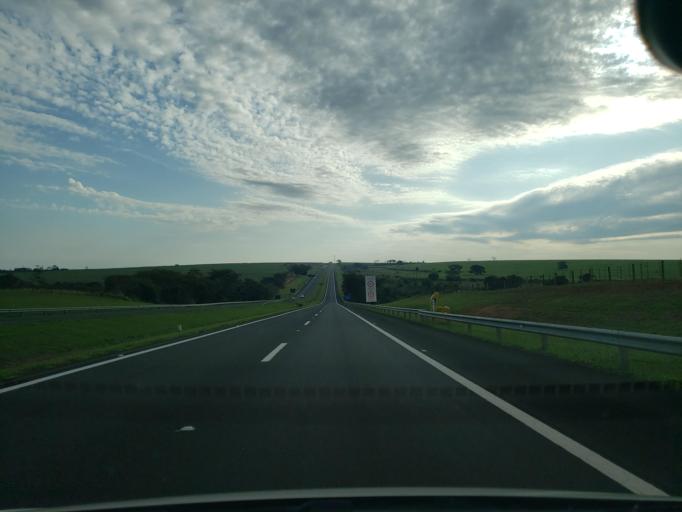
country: BR
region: Sao Paulo
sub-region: Guararapes
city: Guararapes
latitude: -21.2096
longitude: -50.7380
